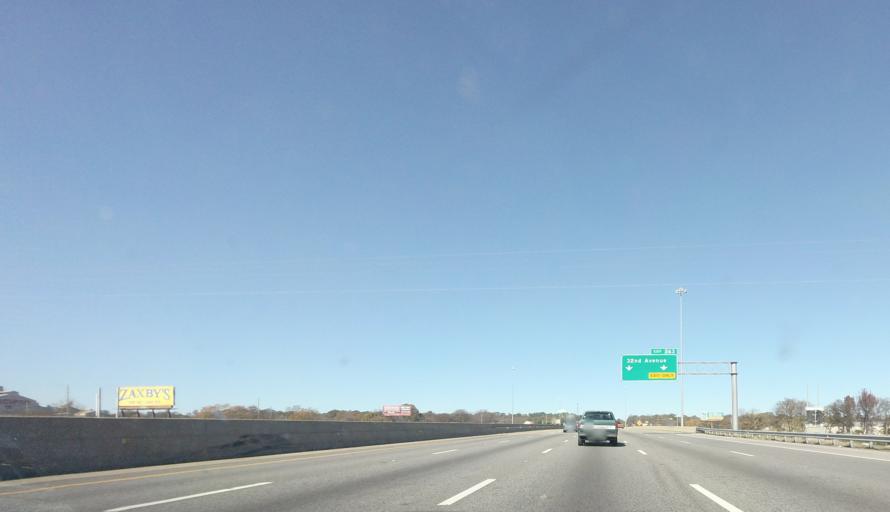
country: US
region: Alabama
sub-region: Jefferson County
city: Birmingham
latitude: 33.5448
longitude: -86.8270
